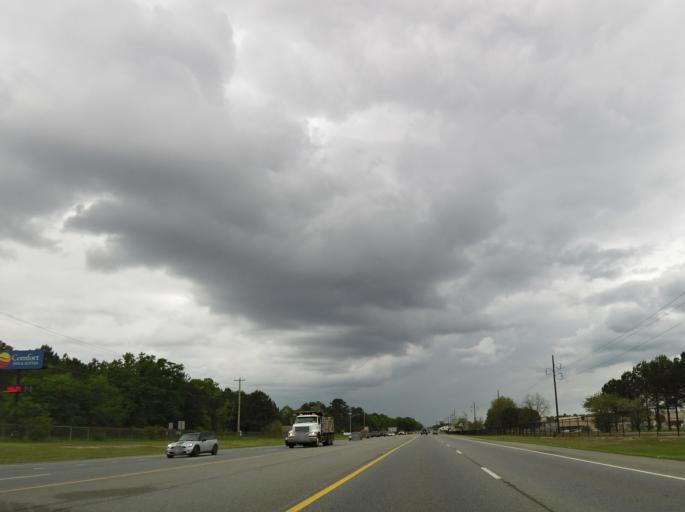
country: US
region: Georgia
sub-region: Houston County
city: Robins Air Force Base
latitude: 32.5967
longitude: -83.5920
